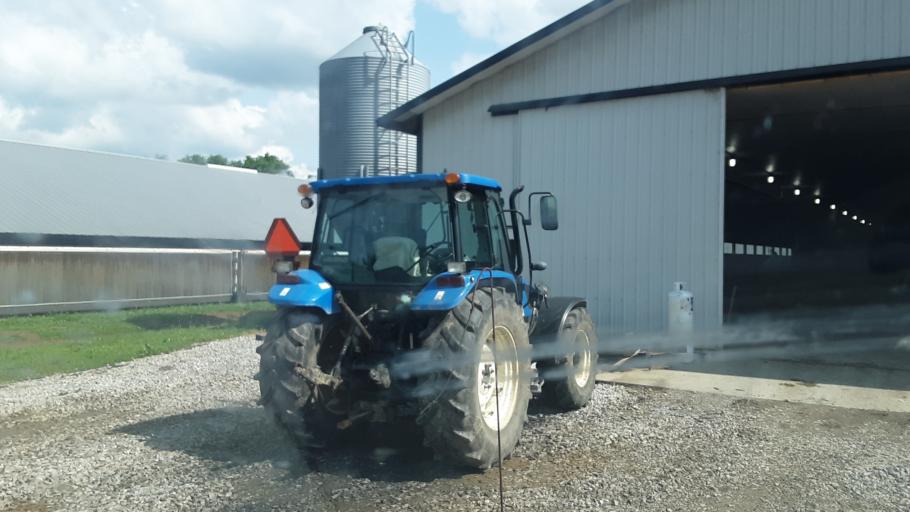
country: US
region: Ohio
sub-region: Knox County
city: Fredericktown
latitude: 40.4595
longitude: -82.6115
